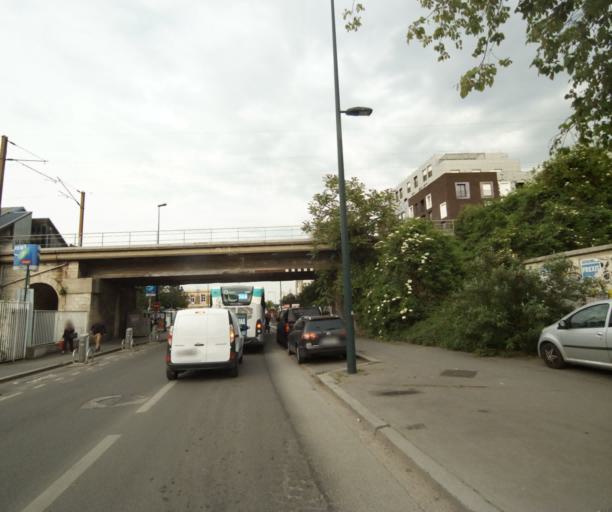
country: FR
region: Ile-de-France
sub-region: Departement des Hauts-de-Seine
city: Gennevilliers
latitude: 48.9197
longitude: 2.3140
